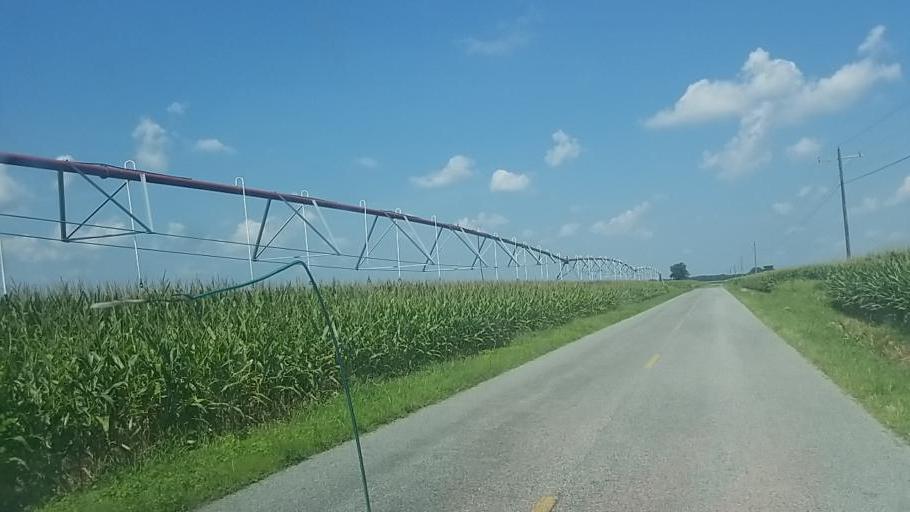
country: US
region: Maryland
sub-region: Worcester County
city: Berlin
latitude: 38.2903
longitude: -75.2433
